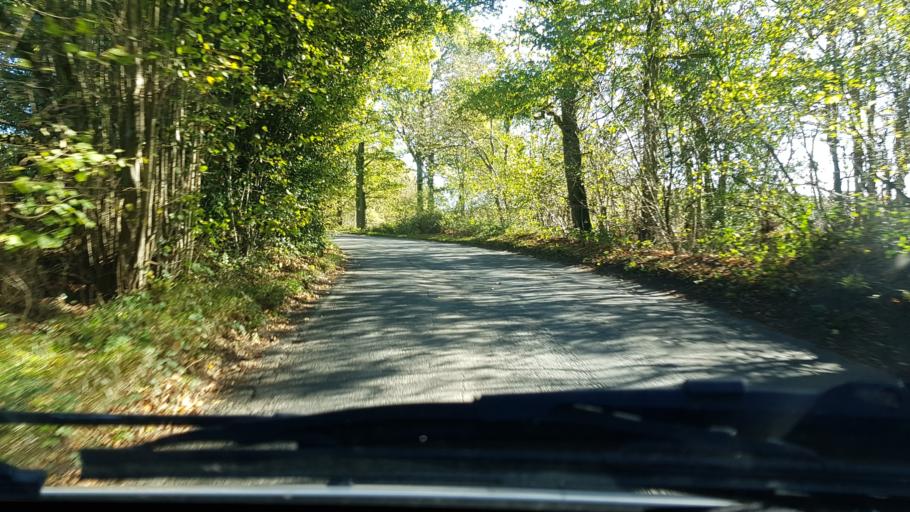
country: GB
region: England
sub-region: Surrey
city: Ockley
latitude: 51.1267
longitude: -0.3952
